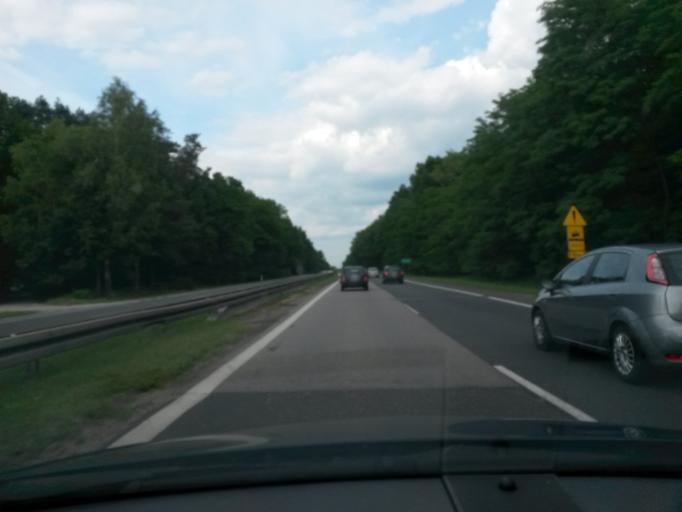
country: PL
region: Lodz Voivodeship
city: Zabia Wola
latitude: 52.0568
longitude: 20.7296
